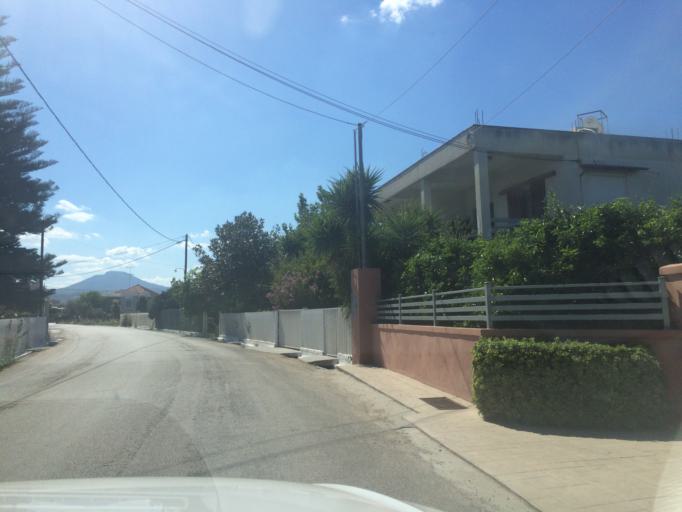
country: GR
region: Peloponnese
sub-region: Nomos Korinthias
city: Vokhaiko
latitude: 37.9490
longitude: 22.7938
